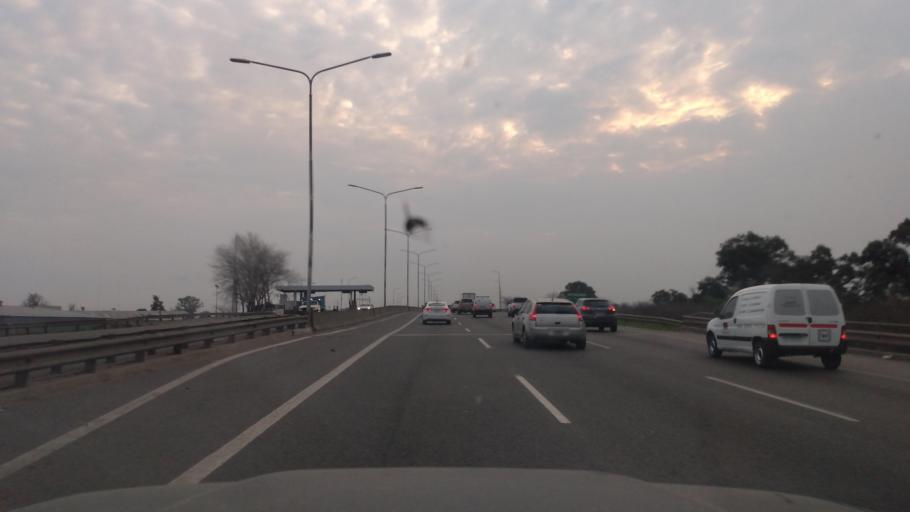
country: AR
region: Buenos Aires
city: Hurlingham
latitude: -34.5681
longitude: -58.6475
